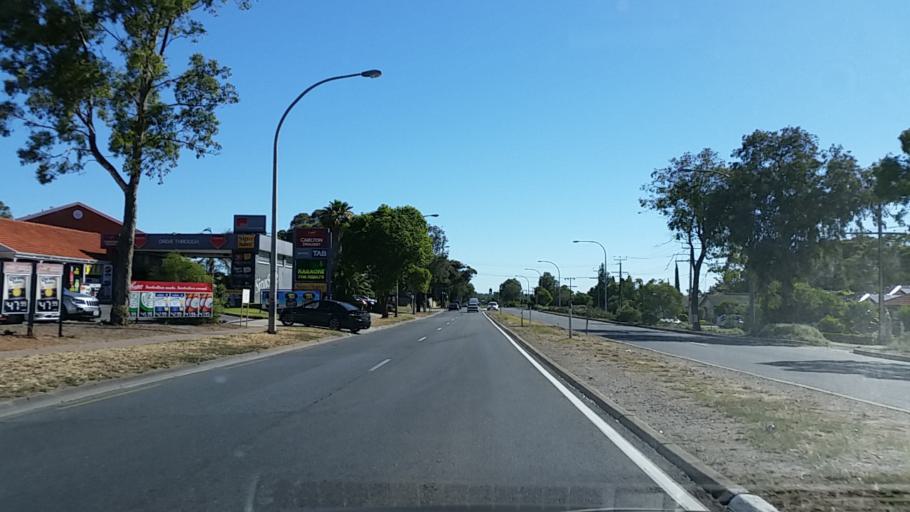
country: AU
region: South Australia
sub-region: Salisbury
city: Salisbury
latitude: -34.7997
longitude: 138.6557
